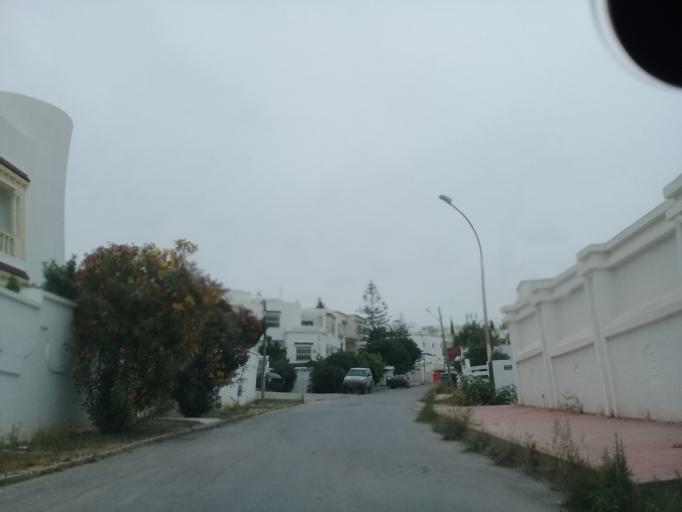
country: TN
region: Tunis
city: Tunis
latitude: 36.8458
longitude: 10.1500
